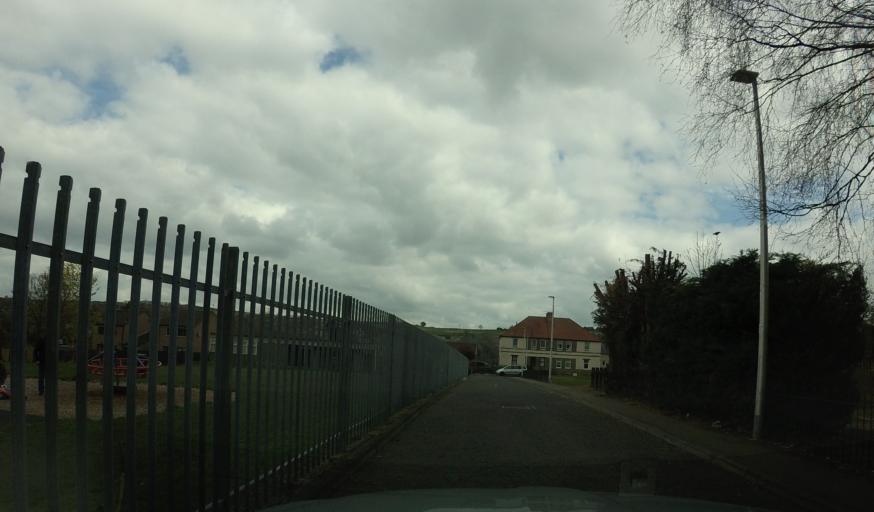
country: GB
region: Scotland
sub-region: Midlothian
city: Gorebridge
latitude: 55.8370
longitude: -3.0491
